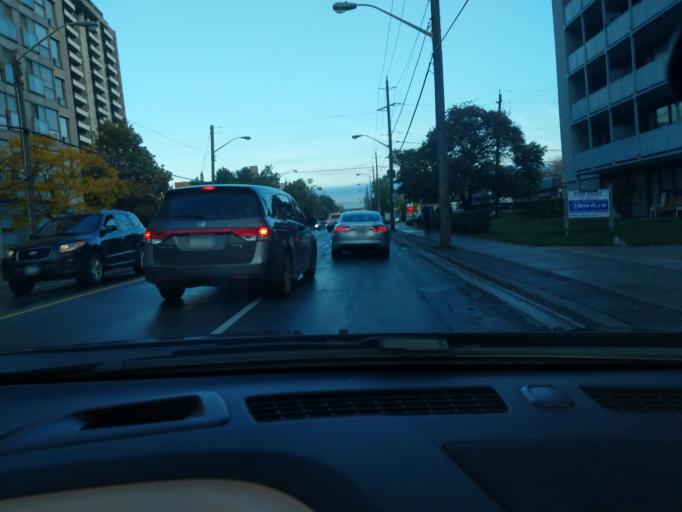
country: CA
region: Ontario
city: Toronto
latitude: 43.7316
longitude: -79.4326
